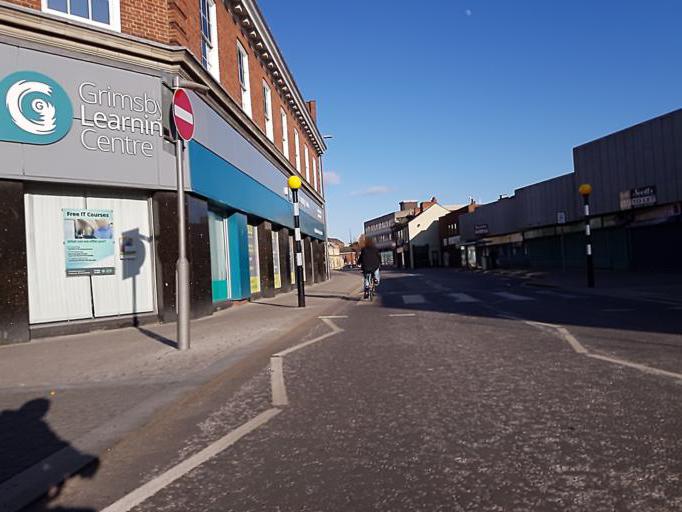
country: GB
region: England
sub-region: North East Lincolnshire
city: Grimsby
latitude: 53.5648
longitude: -0.0857
